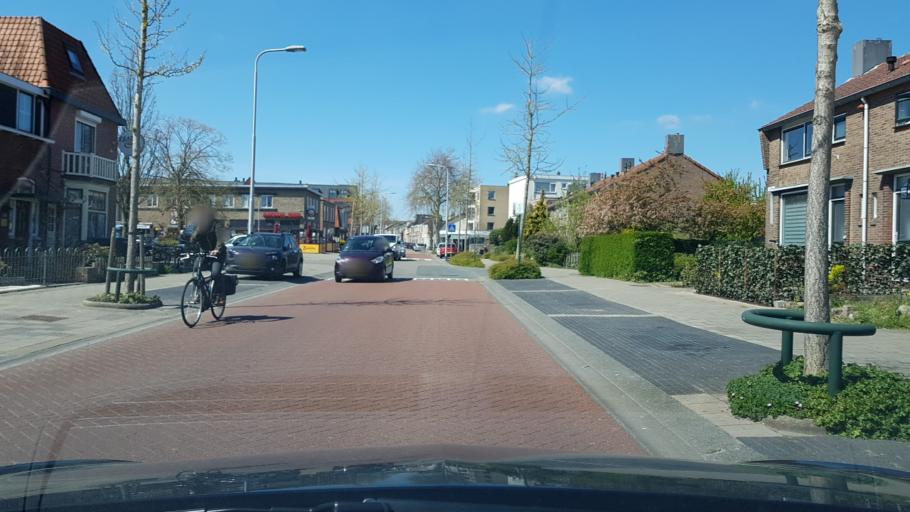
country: NL
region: South Holland
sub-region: Gemeente Hillegom
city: Hillegom
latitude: 52.2917
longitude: 4.5850
